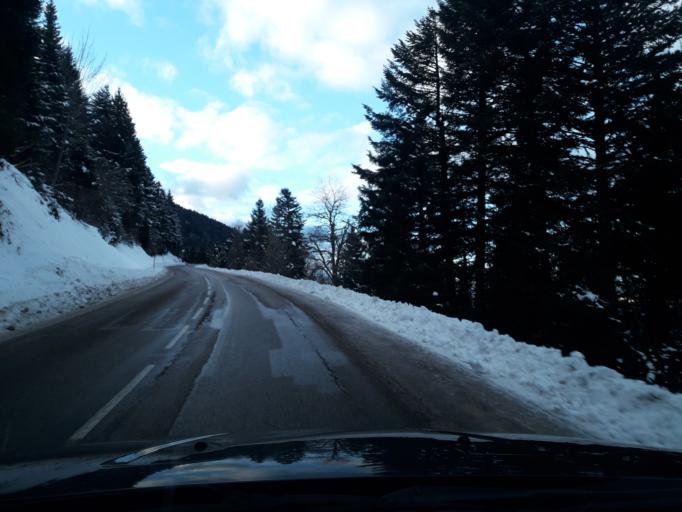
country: FR
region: Rhone-Alpes
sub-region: Departement de l'Isere
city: Revel
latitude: 45.1440
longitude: 5.8800
